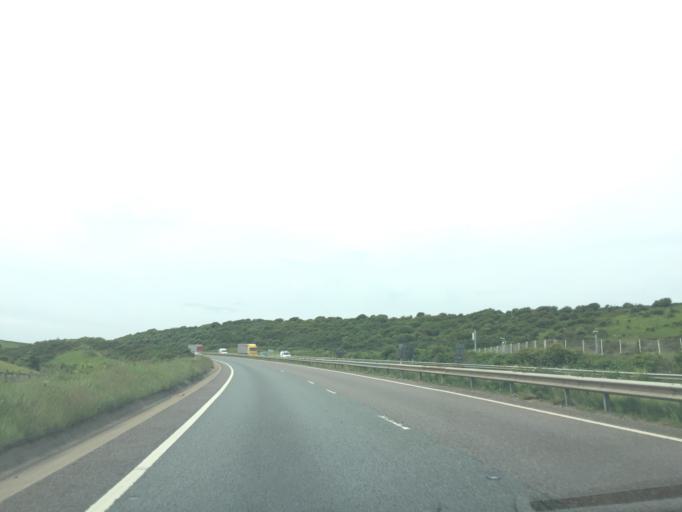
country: GB
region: England
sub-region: Kent
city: Dover
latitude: 51.1101
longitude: 1.2805
